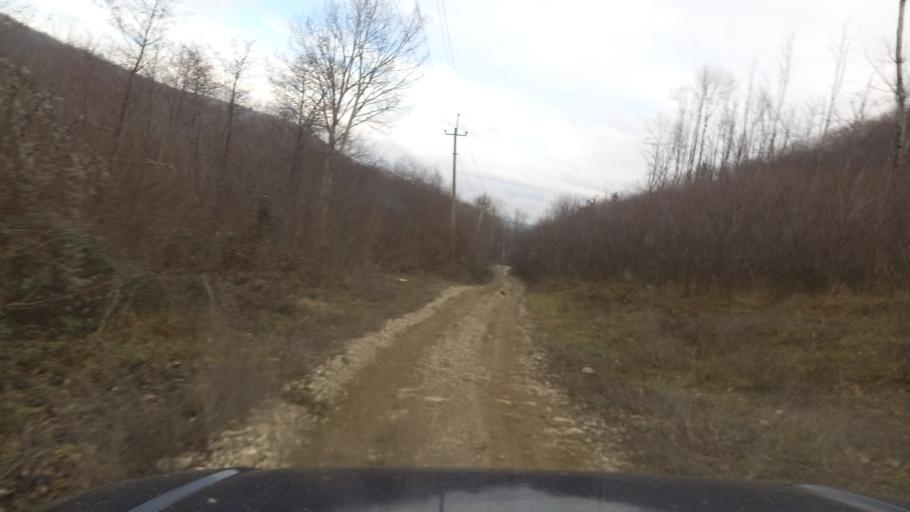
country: RU
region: Krasnodarskiy
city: Neftegorsk
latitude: 44.2152
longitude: 39.7145
